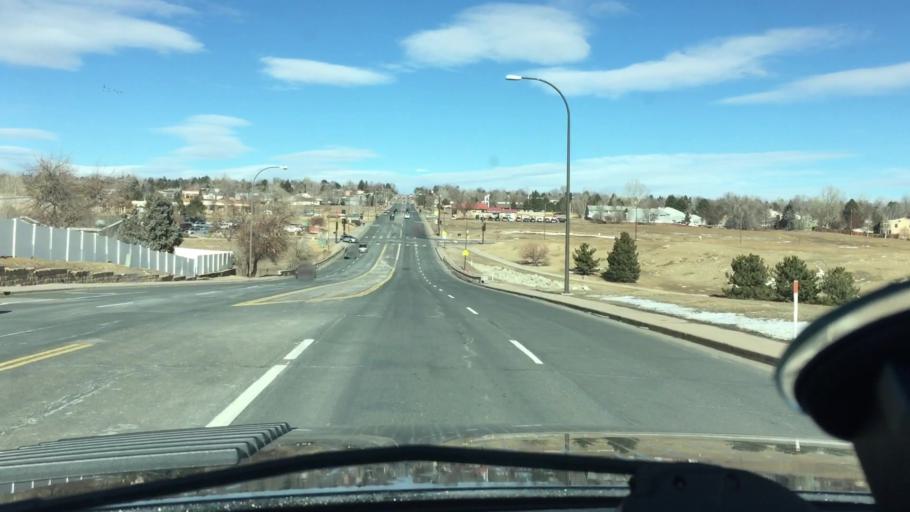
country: US
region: Colorado
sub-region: Adams County
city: Federal Heights
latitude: 39.8646
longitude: -104.9966
